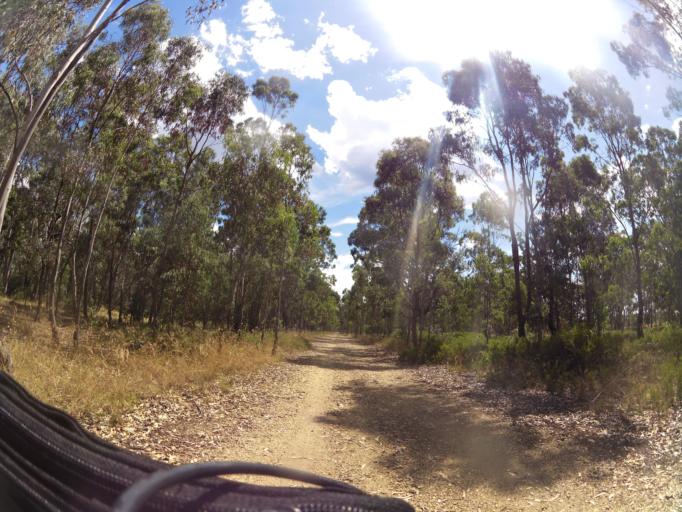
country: AU
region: Victoria
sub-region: Wellington
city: Heyfield
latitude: -37.9830
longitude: 146.7272
